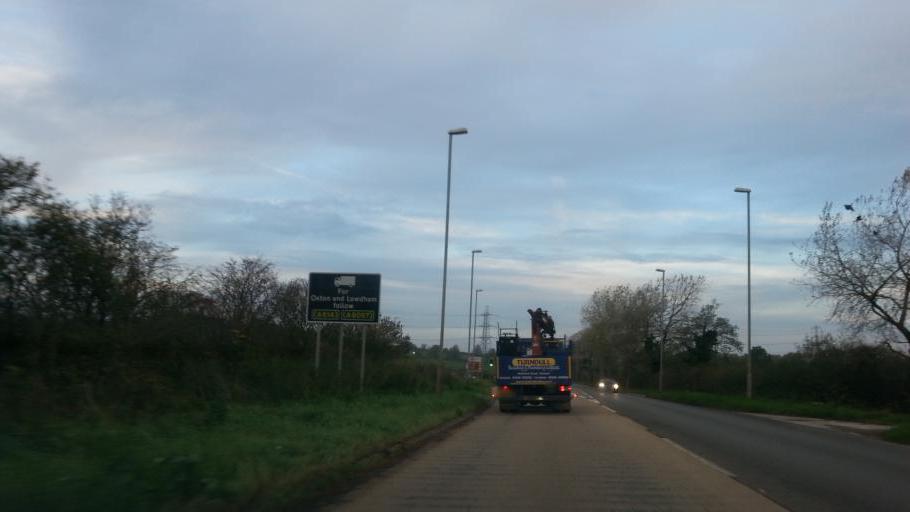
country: GB
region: England
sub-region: Nottinghamshire
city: Farndon
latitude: 53.0892
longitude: -0.8744
